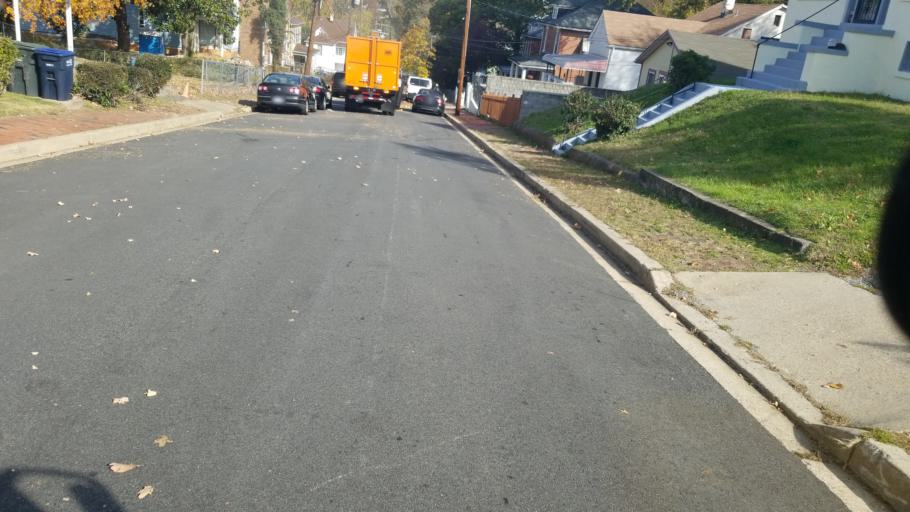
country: US
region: Maryland
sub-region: Prince George's County
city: Hillcrest Heights
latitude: 38.8613
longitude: -76.9878
